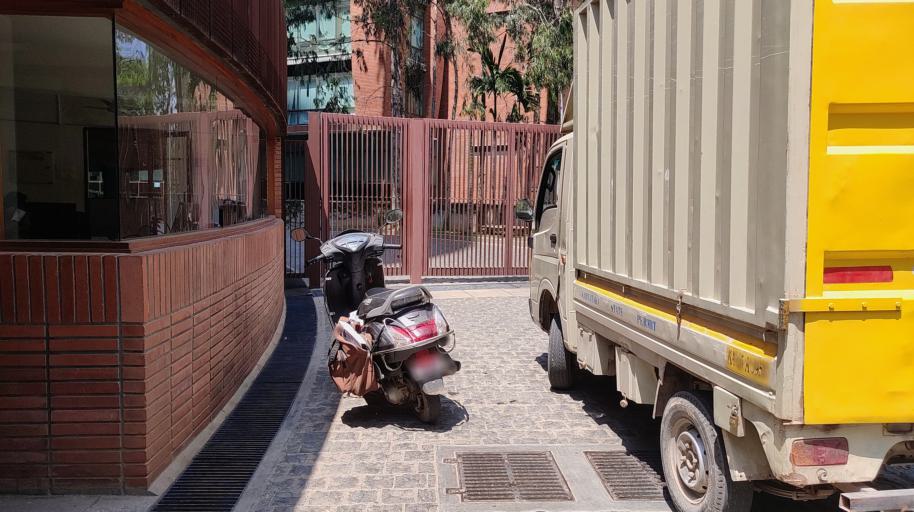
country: IN
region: Karnataka
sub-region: Bangalore Rural
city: Hoskote
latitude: 12.9829
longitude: 77.7217
